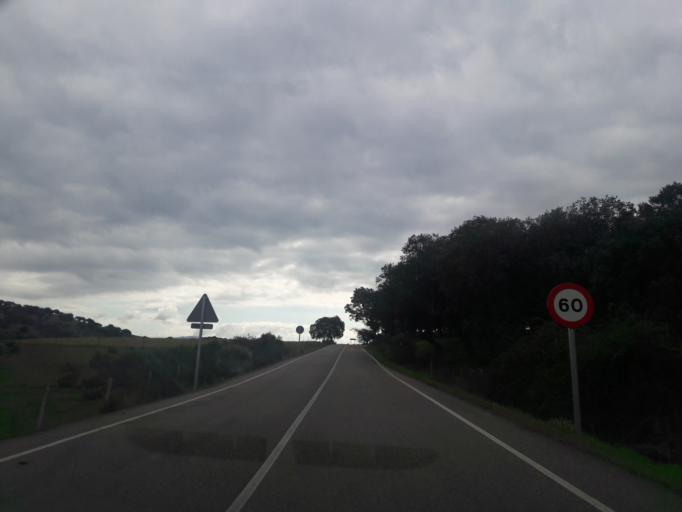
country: ES
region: Castille and Leon
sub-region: Provincia de Salamanca
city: Serradilla del Arroyo
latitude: 40.5205
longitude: -6.4022
